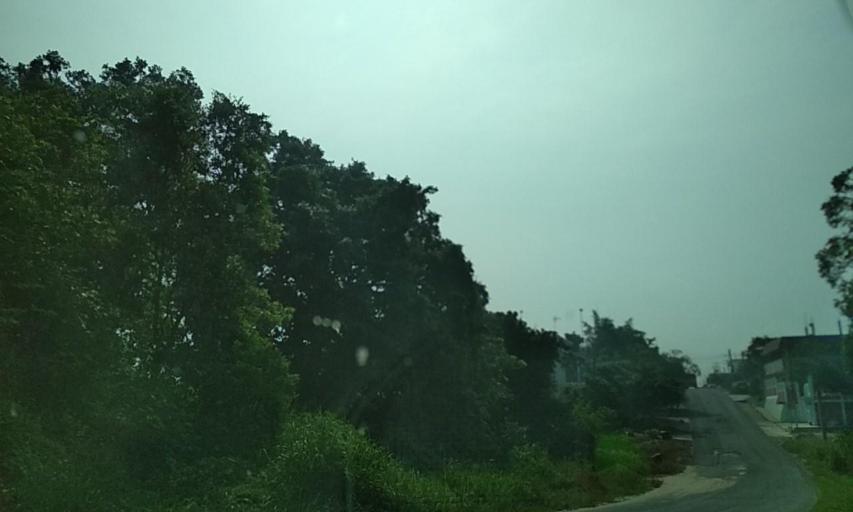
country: MX
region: Veracruz
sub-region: Martinez de la Torre
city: El Progreso
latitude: 20.1492
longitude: -97.0663
